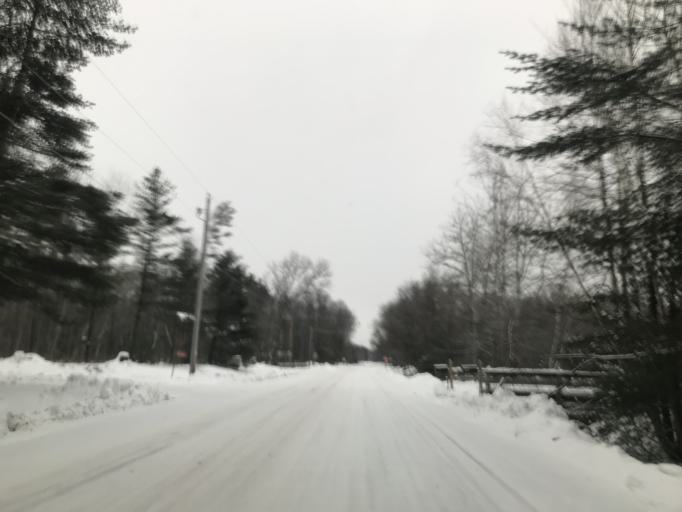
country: US
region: Wisconsin
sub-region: Marinette County
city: Peshtigo
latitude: 45.0413
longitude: -87.7192
